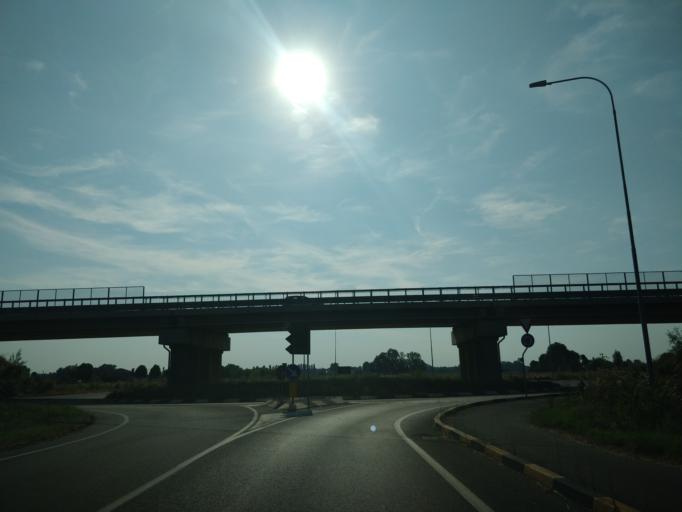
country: IT
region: Emilia-Romagna
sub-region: Provincia di Bologna
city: Progresso
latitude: 44.5622
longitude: 11.3450
